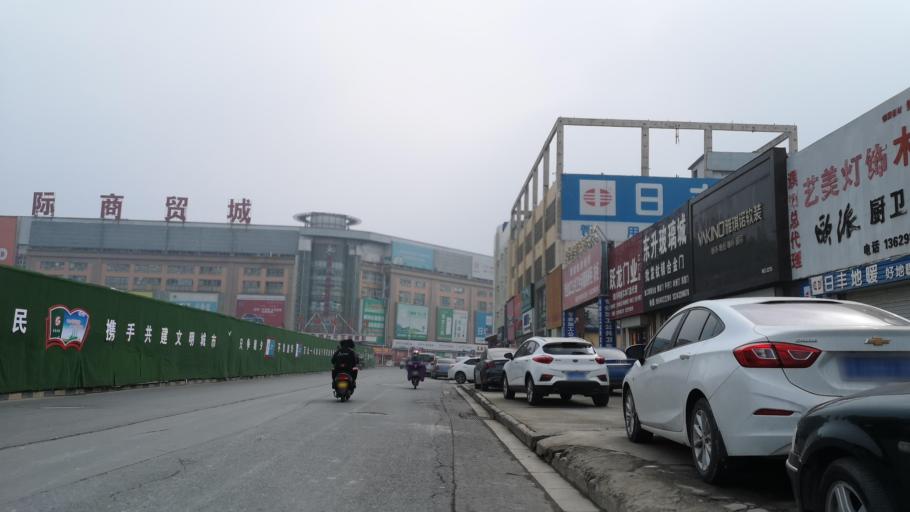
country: CN
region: Henan Sheng
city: Zhongyuanlu
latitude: 35.7752
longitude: 115.0530
